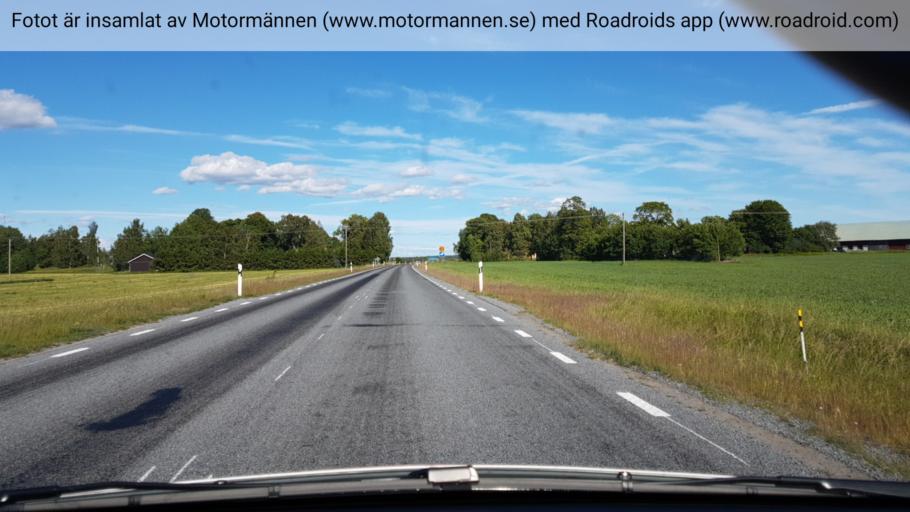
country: SE
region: Vaestra Goetaland
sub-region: Toreboda Kommun
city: Toereboda
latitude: 58.7055
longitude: 14.0734
